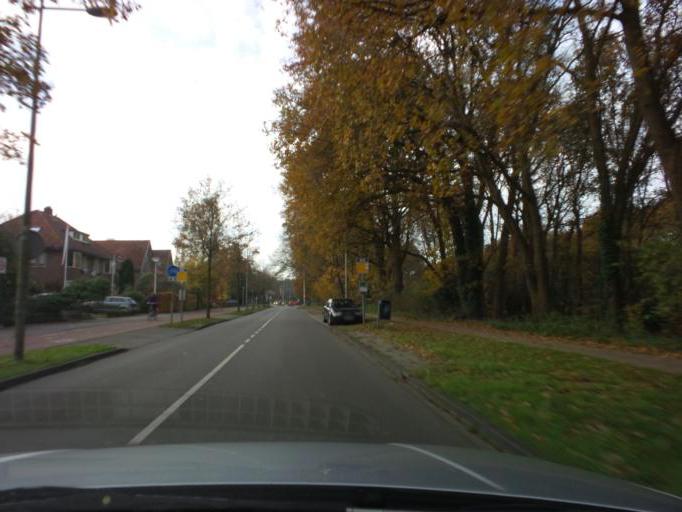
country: NL
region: Utrecht
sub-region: Gemeente Amersfoort
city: Amersfoort
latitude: 52.1518
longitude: 5.3578
